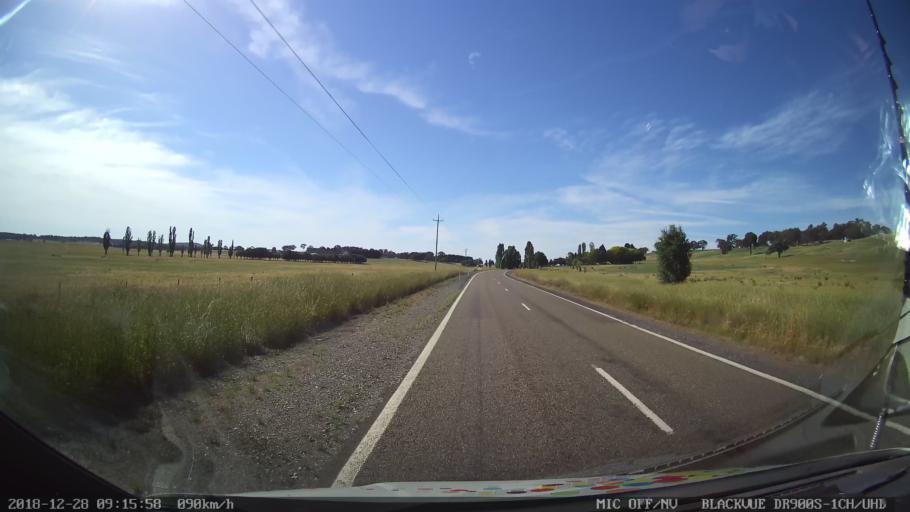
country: AU
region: New South Wales
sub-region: Upper Lachlan Shire
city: Crookwell
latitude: -34.3023
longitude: 149.3530
